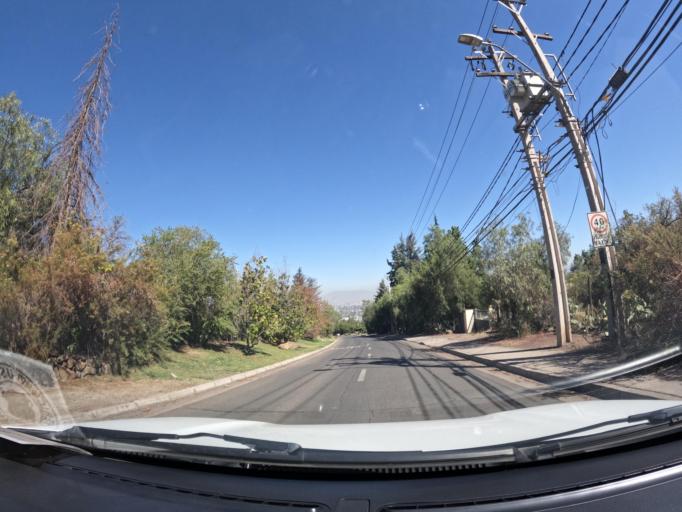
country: CL
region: Santiago Metropolitan
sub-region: Provincia de Santiago
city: Villa Presidente Frei, Nunoa, Santiago, Chile
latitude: -33.4740
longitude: -70.5224
